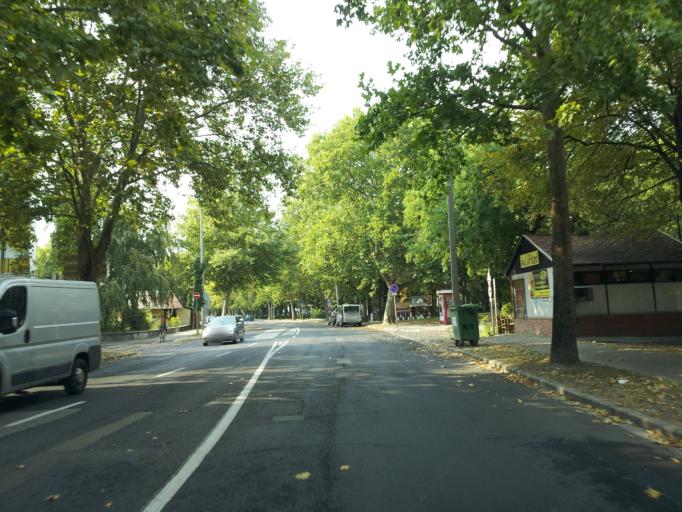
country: HU
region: Gyor-Moson-Sopron
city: Gyor
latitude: 47.6699
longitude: 17.6466
